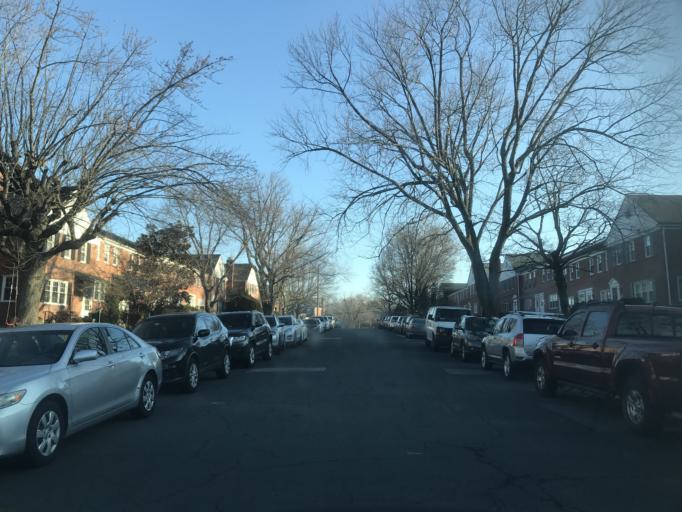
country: US
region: Maryland
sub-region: Baltimore County
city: Towson
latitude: 39.3874
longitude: -76.5762
